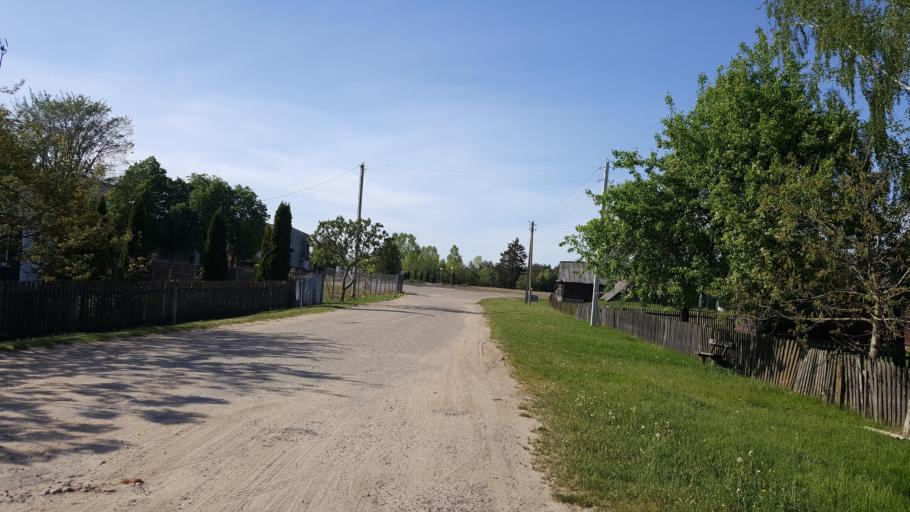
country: BY
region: Brest
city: Kamyanyets
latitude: 52.3336
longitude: 23.9110
